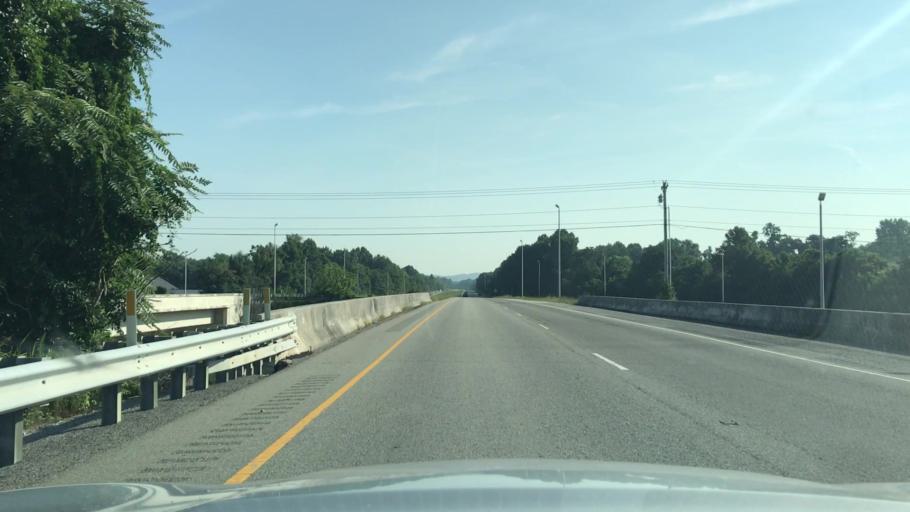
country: US
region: Tennessee
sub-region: Putnam County
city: Cookeville
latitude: 36.1516
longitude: -85.4742
